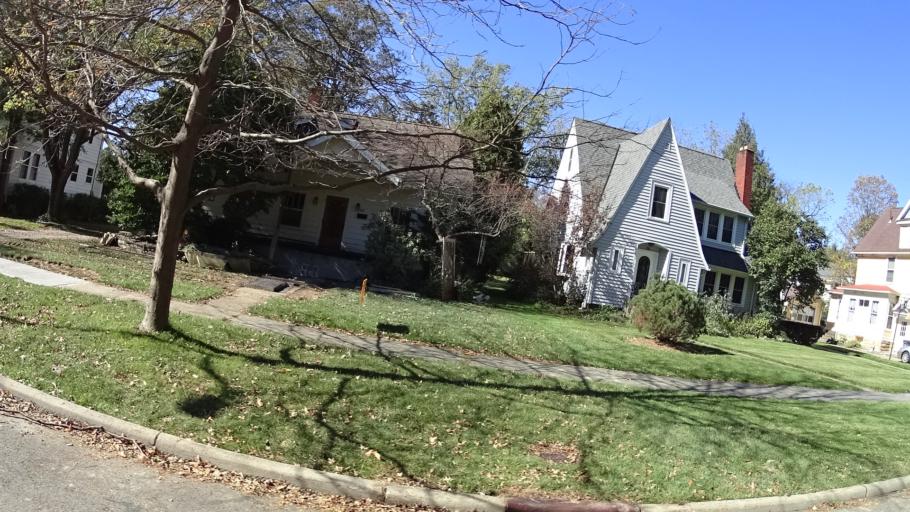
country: US
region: Ohio
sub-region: Lorain County
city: Oberlin
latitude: 41.2907
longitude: -82.2074
